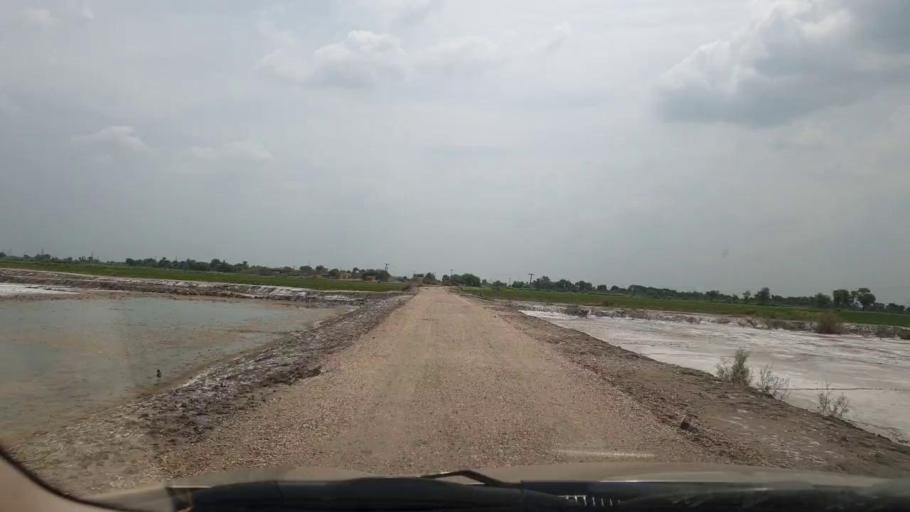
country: PK
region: Sindh
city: Larkana
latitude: 27.5381
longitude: 68.1408
